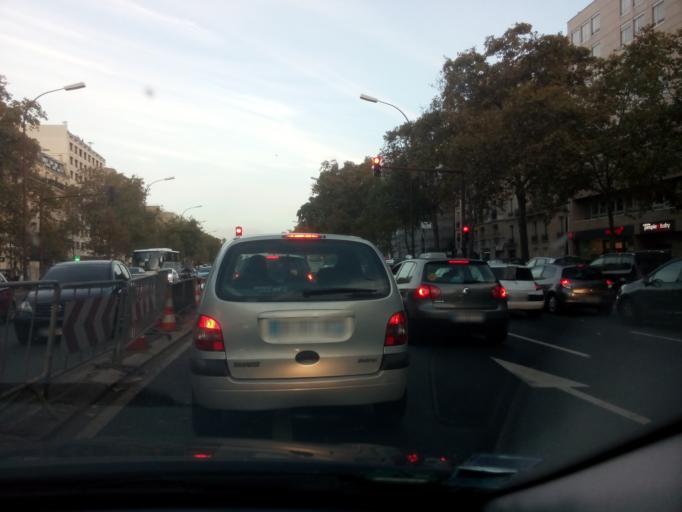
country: FR
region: Ile-de-France
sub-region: Departement des Hauts-de-Seine
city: Neuilly-sur-Seine
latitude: 48.8818
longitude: 2.2694
